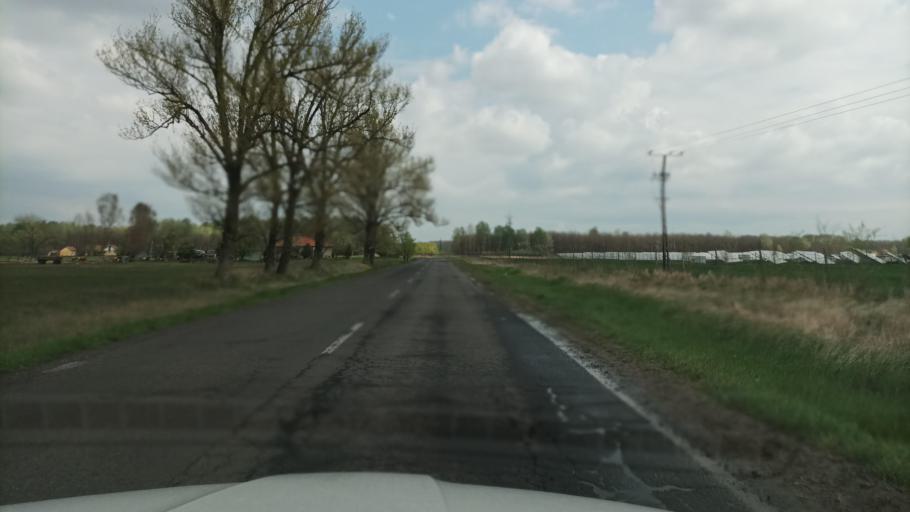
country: HU
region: Pest
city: Nagykoros
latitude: 47.0521
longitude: 19.8439
